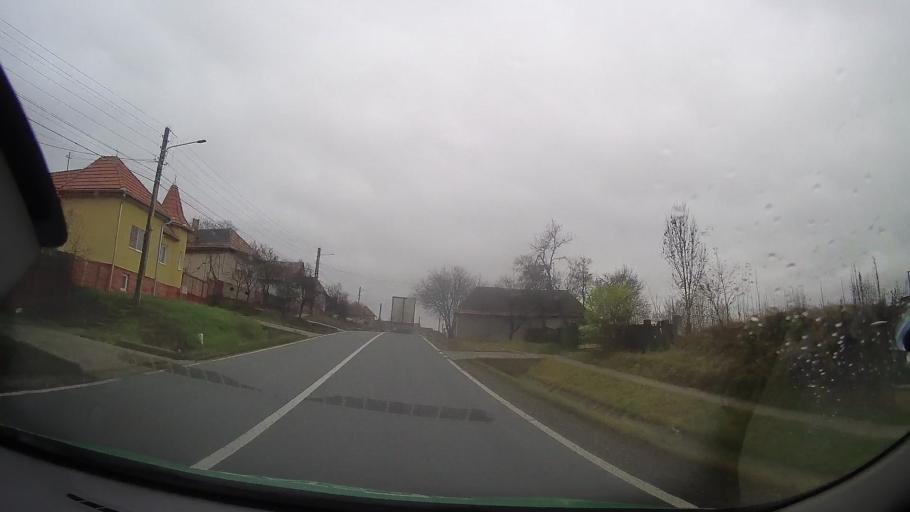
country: RO
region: Mures
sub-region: Comuna Lunca
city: Lunca
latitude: 46.8532
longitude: 24.5722
